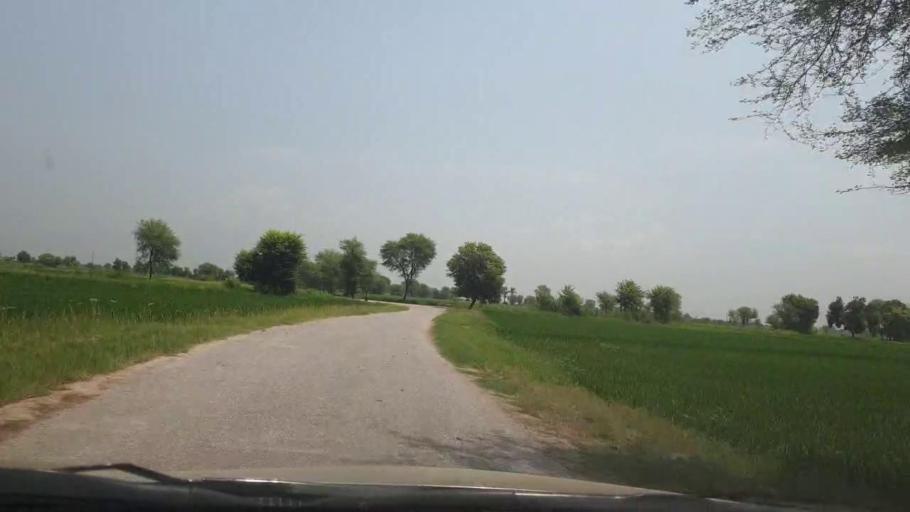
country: PK
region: Sindh
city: Ratodero
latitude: 27.7353
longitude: 68.3019
